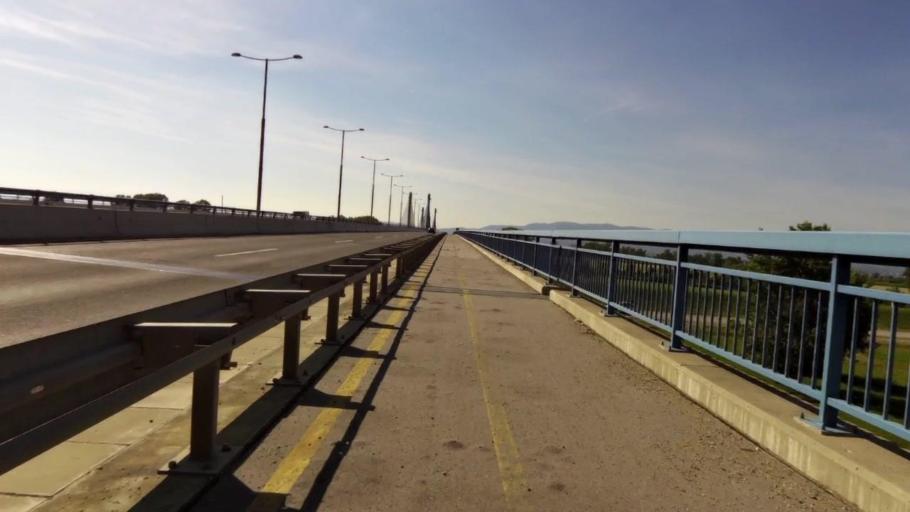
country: HR
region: Zagrebacka
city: Micevec
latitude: 45.7687
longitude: 16.0733
